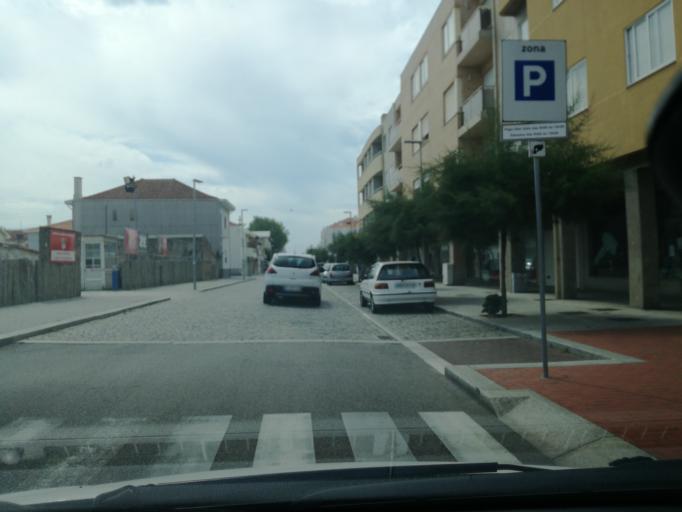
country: PT
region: Aveiro
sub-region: Espinho
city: Espinho
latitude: 41.0067
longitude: -8.6399
